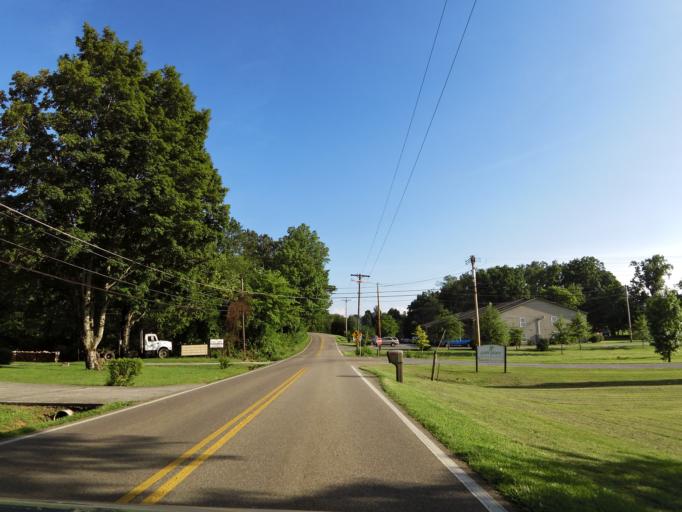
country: US
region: Tennessee
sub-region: Blount County
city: Maryville
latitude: 35.7096
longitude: -83.9688
